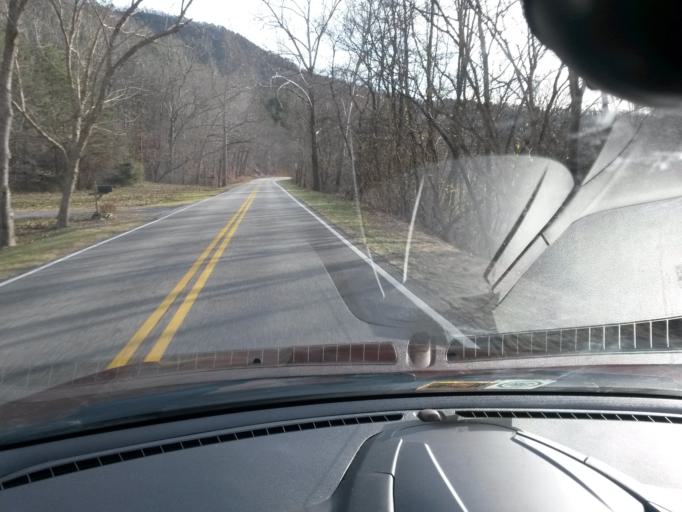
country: US
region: Virginia
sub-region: Alleghany County
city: Clifton Forge
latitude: 37.9019
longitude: -79.7404
